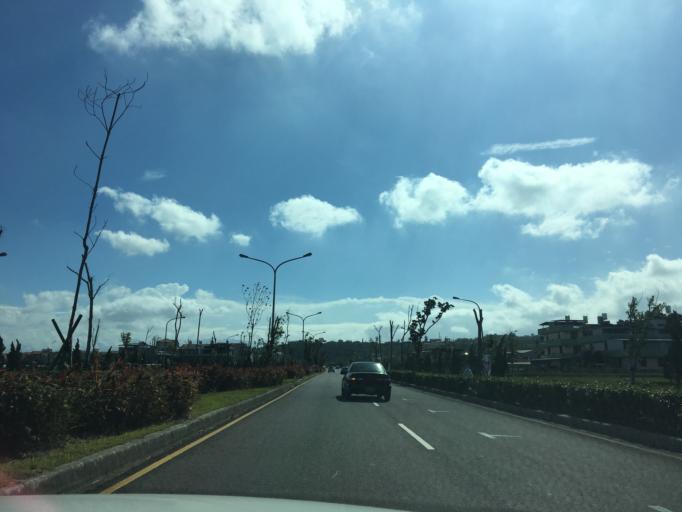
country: TW
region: Taiwan
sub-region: Hsinchu
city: Zhubei
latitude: 24.7849
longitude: 121.0357
